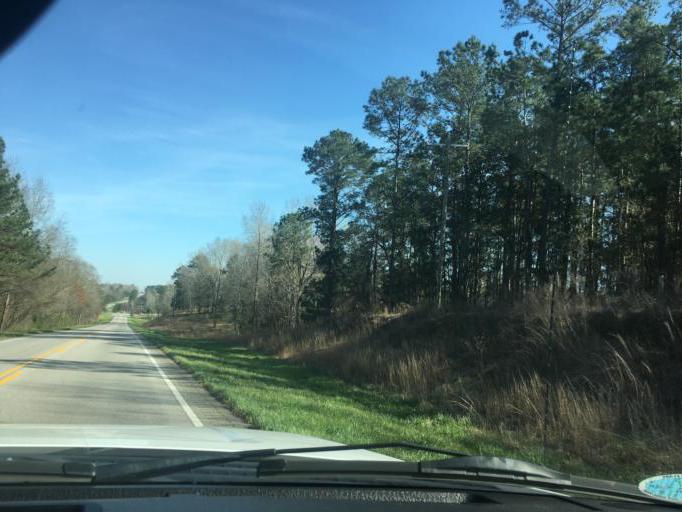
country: US
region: Alabama
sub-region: Lee County
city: Auburn
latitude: 32.4352
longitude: -85.4759
